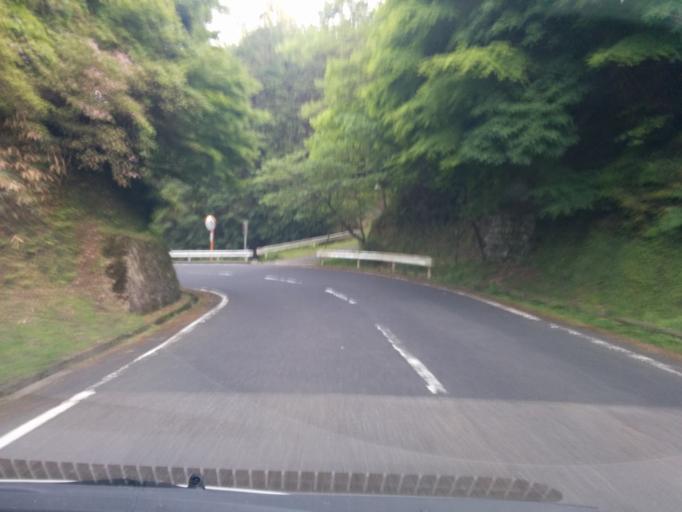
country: JP
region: Shiga Prefecture
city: Kitahama
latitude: 35.1027
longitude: 135.8609
